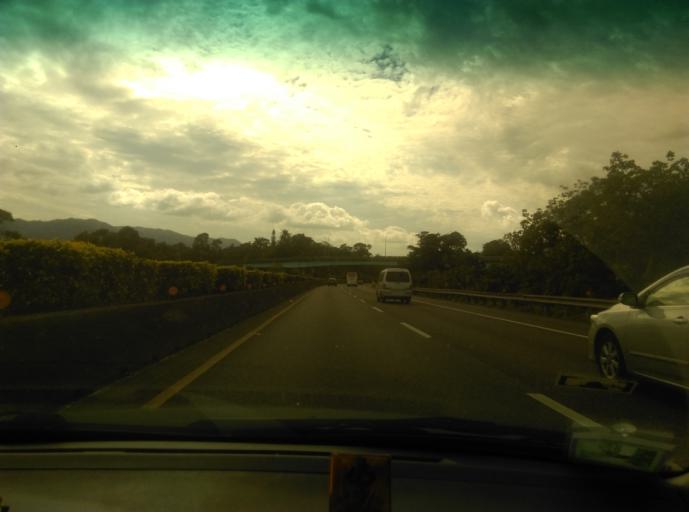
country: TW
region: Taiwan
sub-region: Keelung
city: Keelung
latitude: 25.0995
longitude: 121.7079
